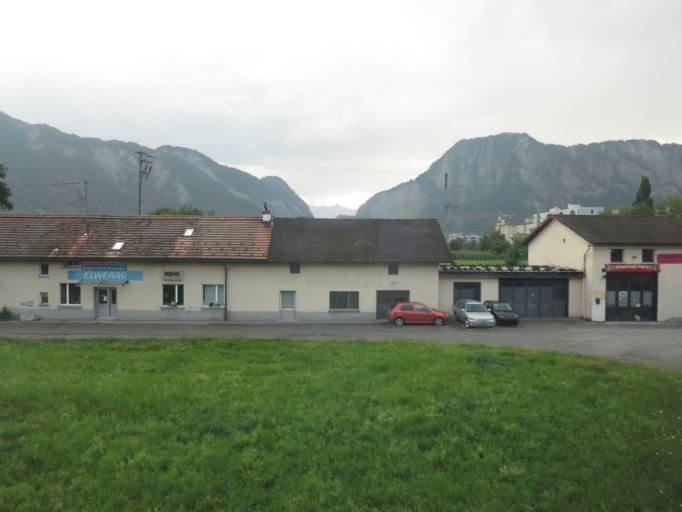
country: CH
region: Grisons
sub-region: Landquart District
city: Landquart
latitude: 46.9693
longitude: 9.5533
